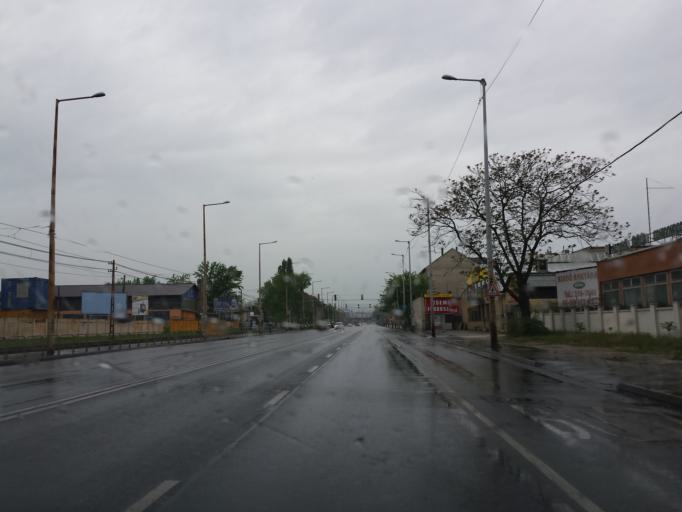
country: HU
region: Budapest
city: Budapest IX. keruelet
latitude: 47.4596
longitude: 19.0830
